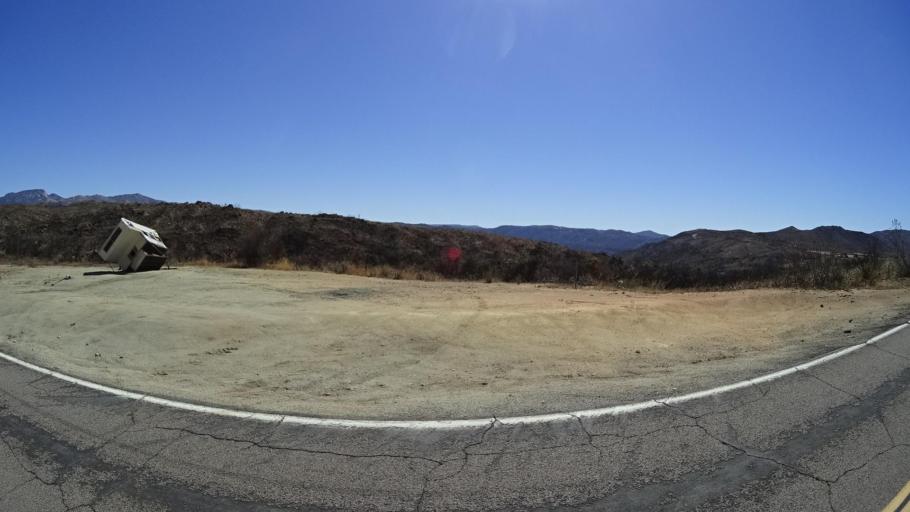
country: US
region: California
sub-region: San Diego County
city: Alpine
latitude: 32.7298
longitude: -116.6953
